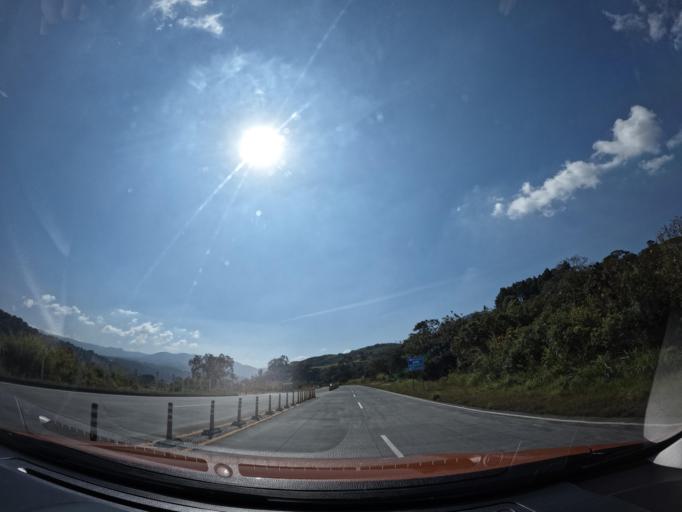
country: GT
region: Guatemala
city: Petapa
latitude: 14.4973
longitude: -90.5444
